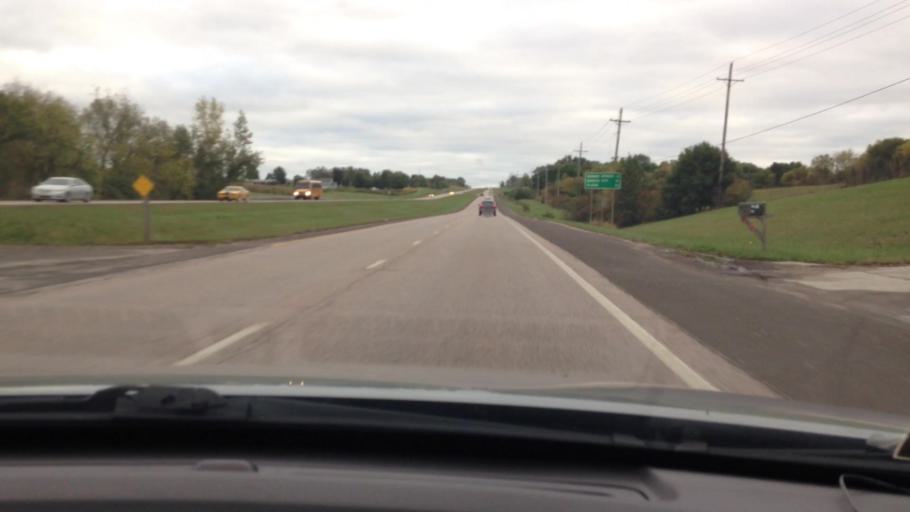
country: US
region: Kansas
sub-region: Leavenworth County
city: Lansing
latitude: 39.2223
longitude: -94.9004
